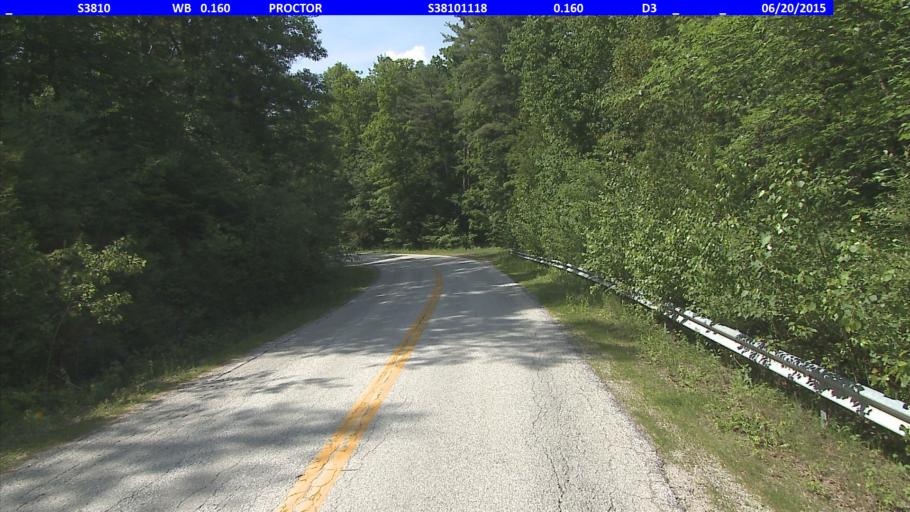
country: US
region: Vermont
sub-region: Rutland County
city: West Rutland
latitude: 43.6672
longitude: -73.0444
